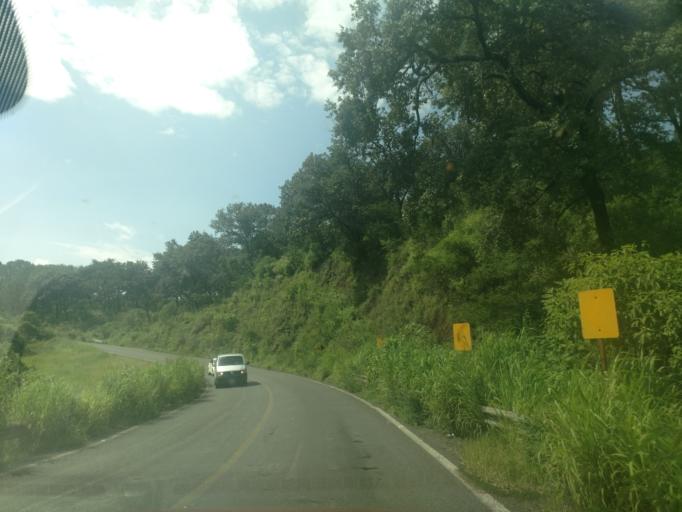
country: MX
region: Jalisco
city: Talpa de Allende
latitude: 20.4412
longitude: -104.7650
